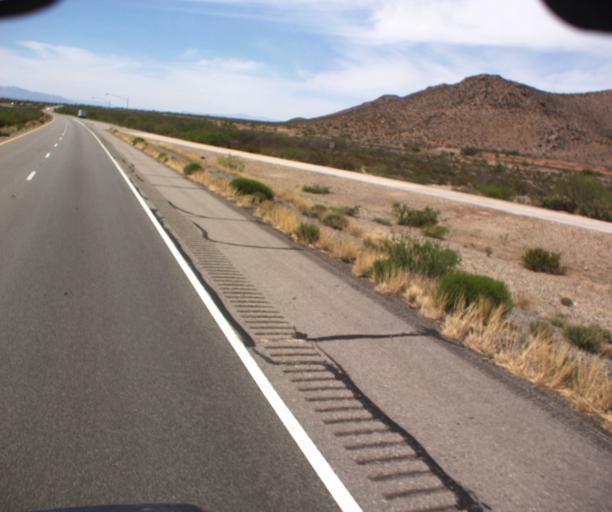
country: US
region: New Mexico
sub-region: Hidalgo County
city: Lordsburg
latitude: 32.2386
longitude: -109.0887
